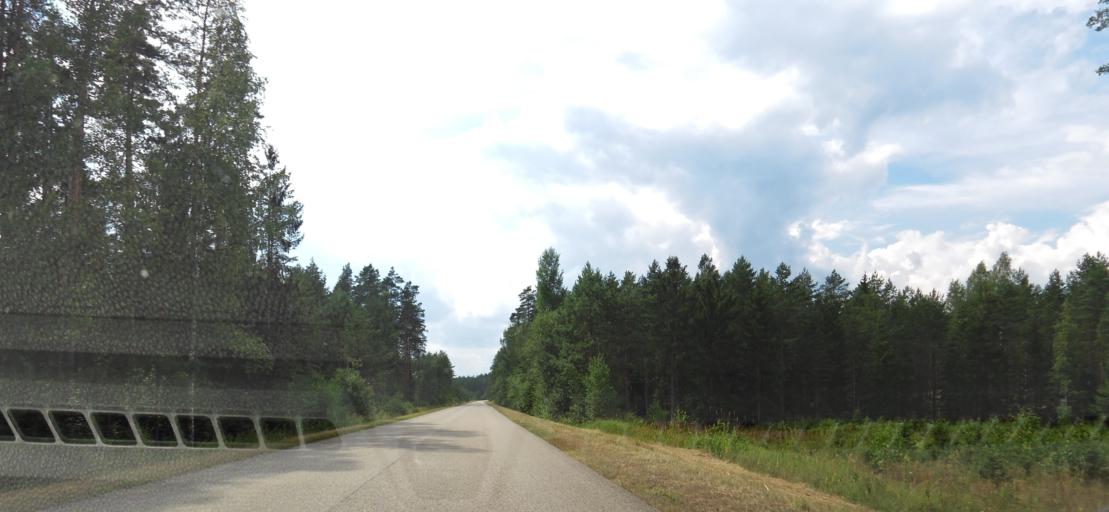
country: LT
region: Alytaus apskritis
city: Druskininkai
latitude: 53.9887
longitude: 24.1416
